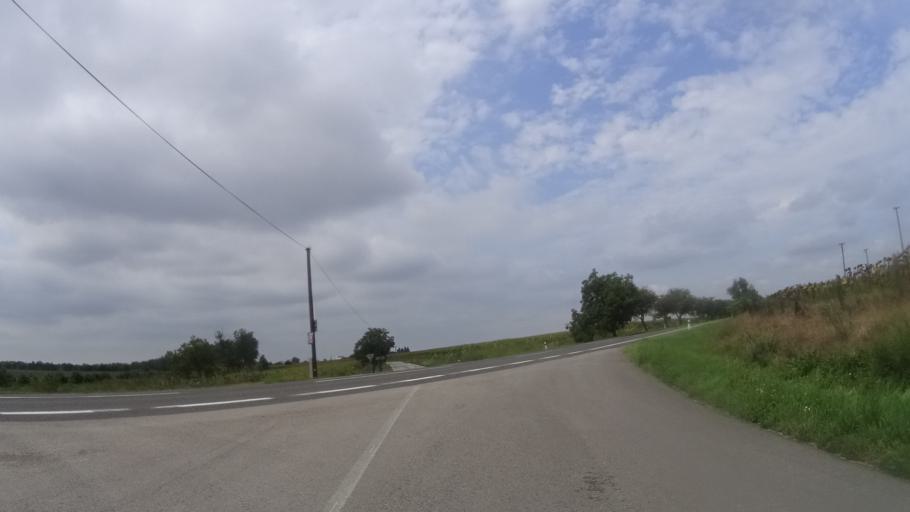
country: HU
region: Komarom-Esztergom
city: Acs
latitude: 47.7698
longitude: 17.9622
